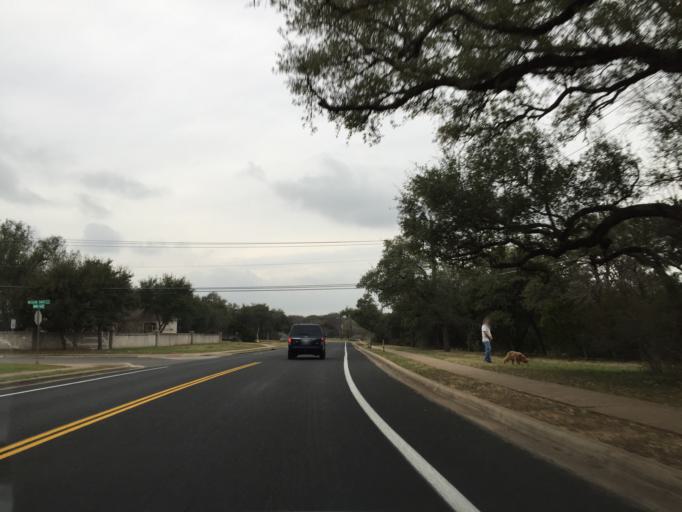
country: US
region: Texas
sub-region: Travis County
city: Lost Creek
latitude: 30.2437
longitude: -97.8351
